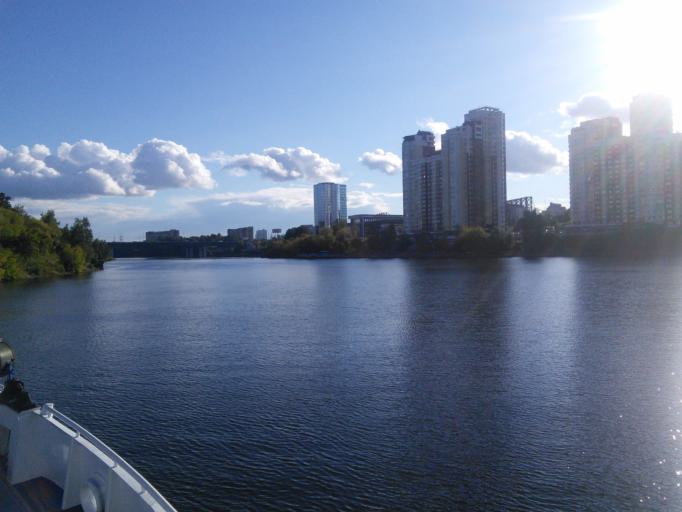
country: RU
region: Moskovskaya
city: Levoberezhnaya
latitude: 55.8892
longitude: 37.4626
